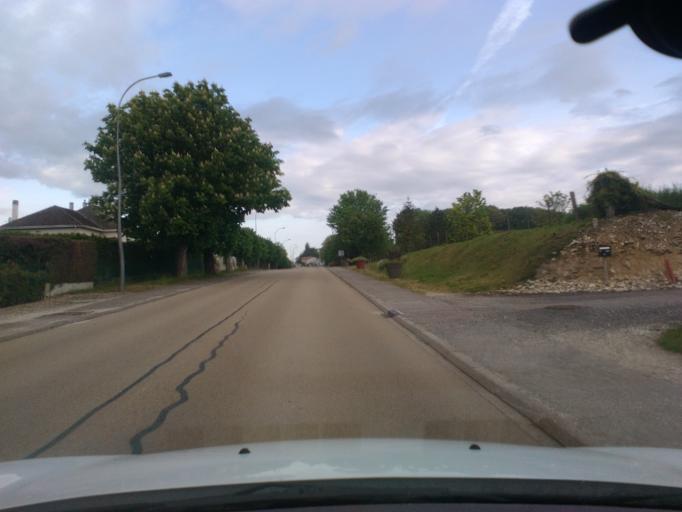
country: FR
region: Champagne-Ardenne
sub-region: Departement de la Haute-Marne
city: Lavilleneuve-au-Roi
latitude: 48.2233
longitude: 4.8928
